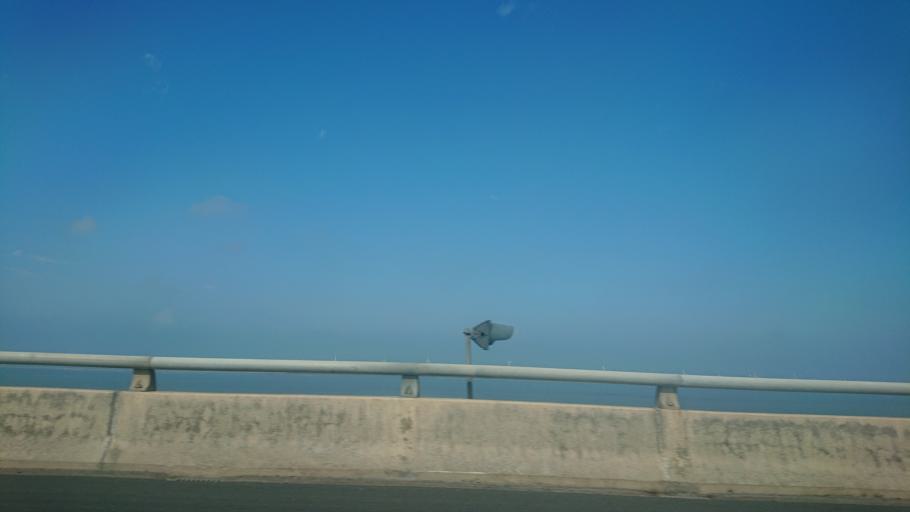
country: TW
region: Taiwan
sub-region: Changhua
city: Chang-hua
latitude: 24.0880
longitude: 120.4278
